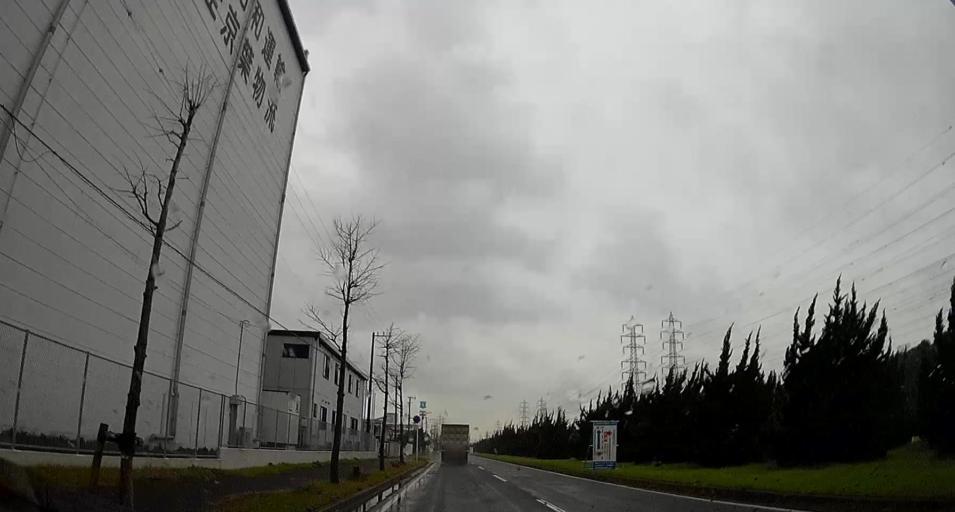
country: JP
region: Chiba
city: Ichihara
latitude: 35.4822
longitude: 140.0369
